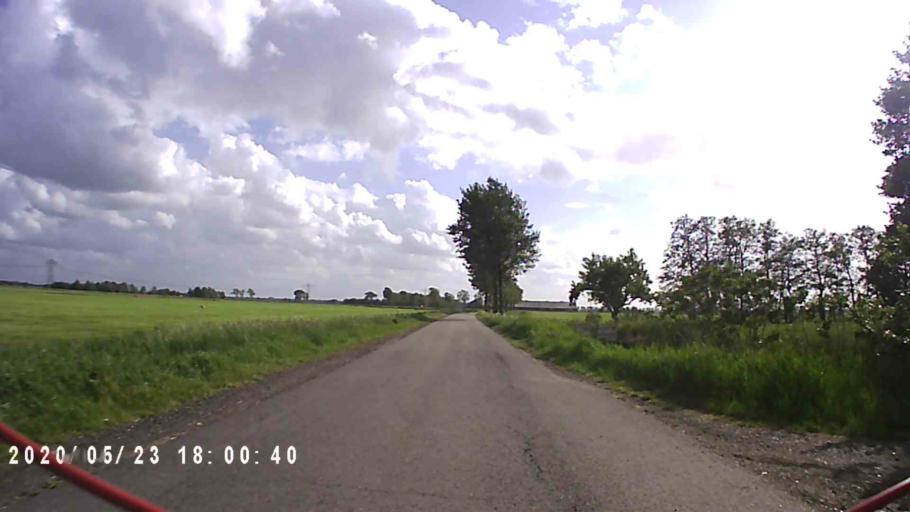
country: NL
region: Groningen
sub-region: Gemeente Slochteren
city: Slochteren
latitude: 53.2501
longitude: 6.7349
